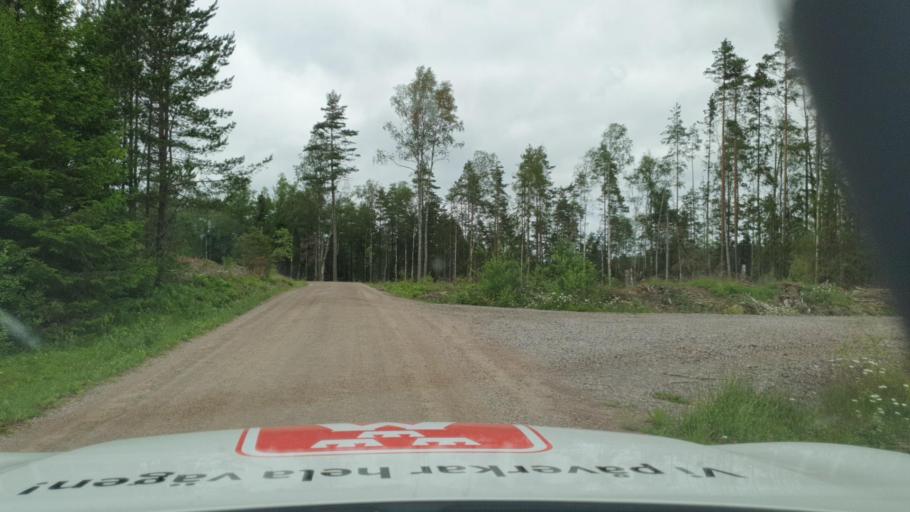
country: SE
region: Vaermland
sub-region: Filipstads Kommun
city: Filipstad
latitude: 59.5860
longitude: 13.9529
